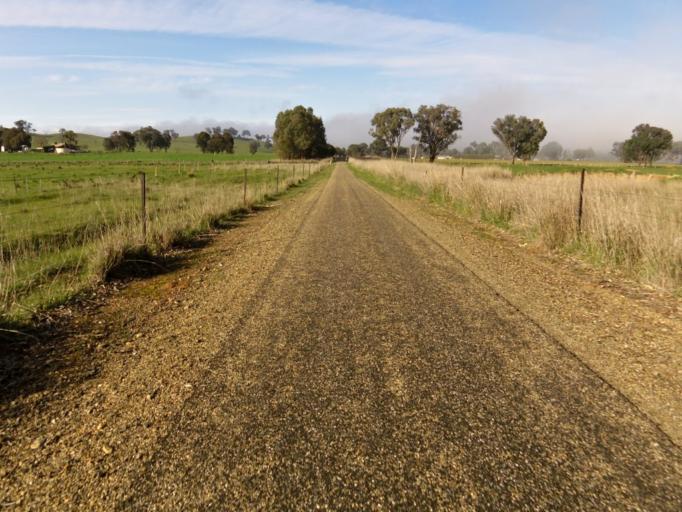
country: AU
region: Victoria
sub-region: Wangaratta
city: Wangaratta
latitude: -36.4364
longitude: 146.5508
